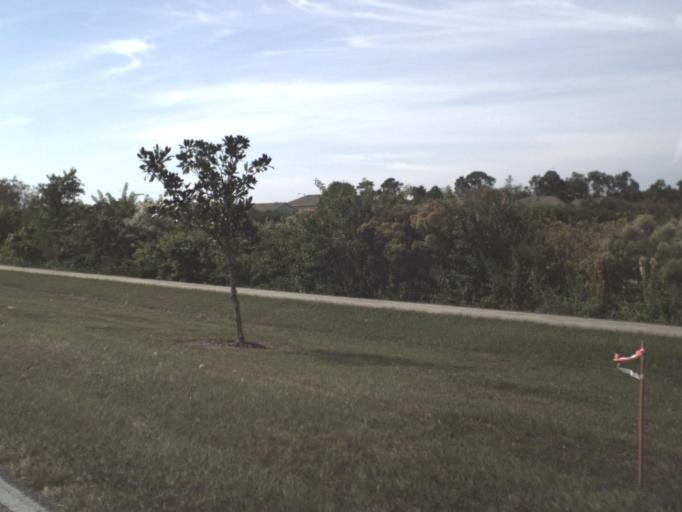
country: US
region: Florida
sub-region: Orange County
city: Hunters Creek
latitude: 28.3861
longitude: -81.4252
